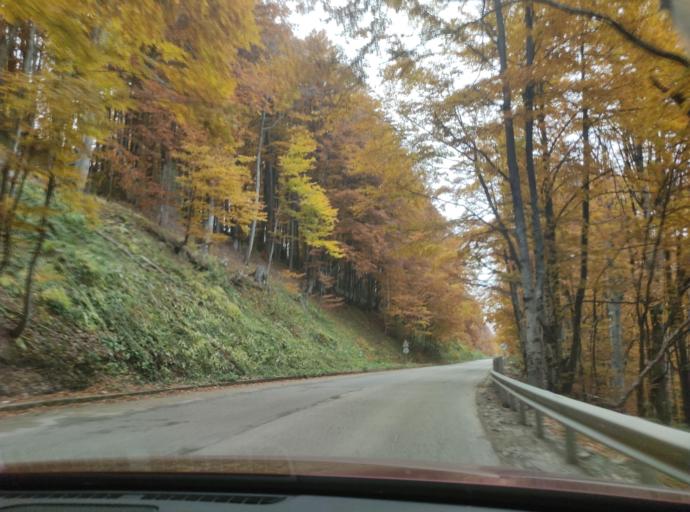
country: BG
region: Montana
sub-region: Obshtina Berkovitsa
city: Berkovitsa
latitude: 43.1238
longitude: 23.1368
